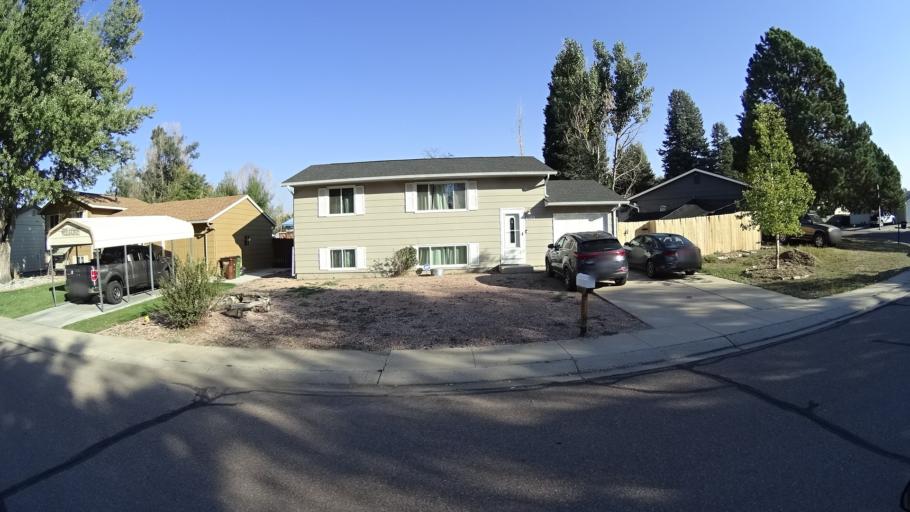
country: US
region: Colorado
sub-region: El Paso County
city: Cimarron Hills
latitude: 38.8886
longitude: -104.7448
